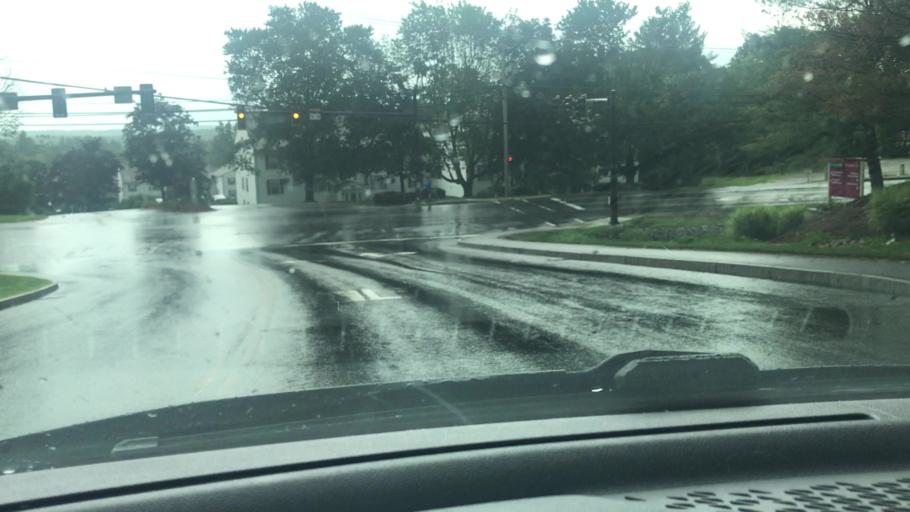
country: US
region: New Hampshire
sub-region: Merrimack County
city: Concord
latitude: 43.1965
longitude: -71.5607
